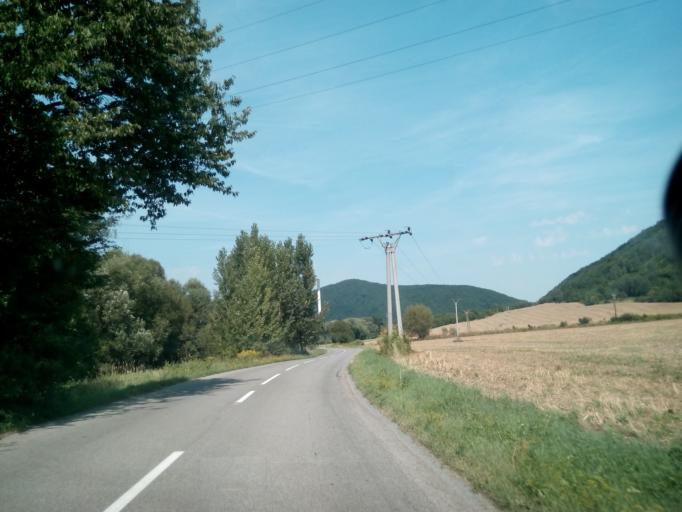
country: SK
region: Kosicky
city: Kosice
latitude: 48.8459
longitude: 21.2279
